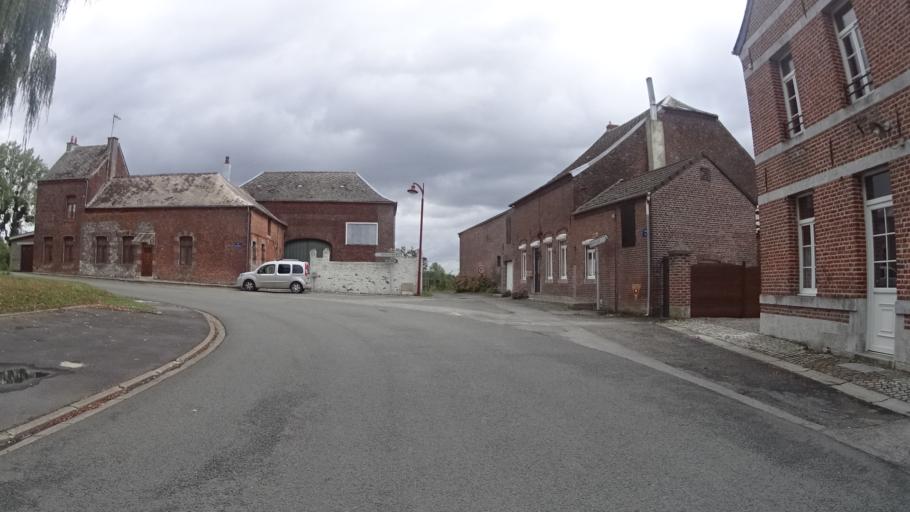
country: FR
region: Nord-Pas-de-Calais
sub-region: Departement du Nord
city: Berlaimont
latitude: 50.1793
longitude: 3.8067
